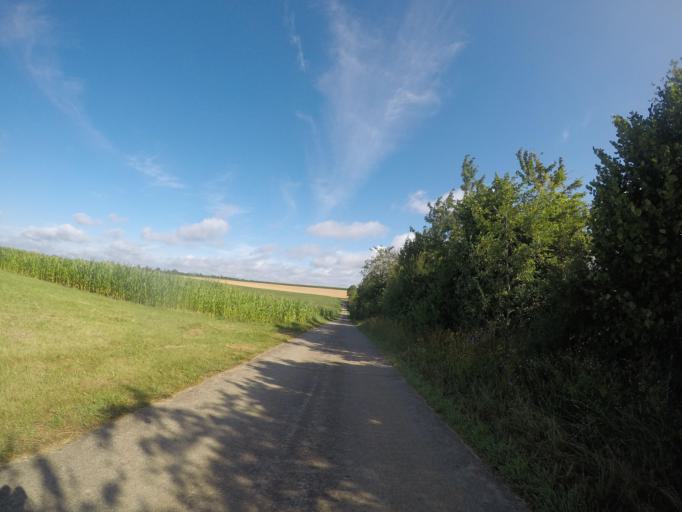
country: DE
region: Baden-Wuerttemberg
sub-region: Tuebingen Region
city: Mehrstetten
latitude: 48.3932
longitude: 9.6304
